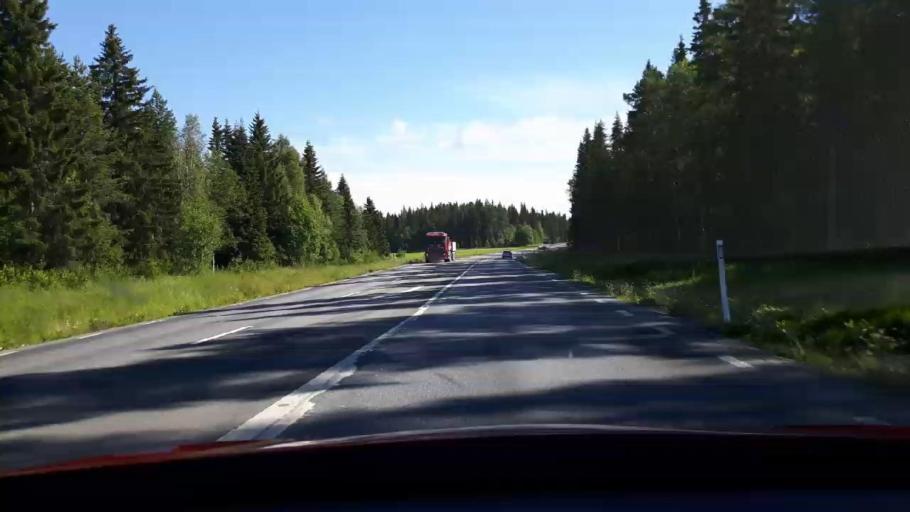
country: SE
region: Jaemtland
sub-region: OEstersunds Kommun
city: Lit
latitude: 63.2422
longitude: 14.7808
